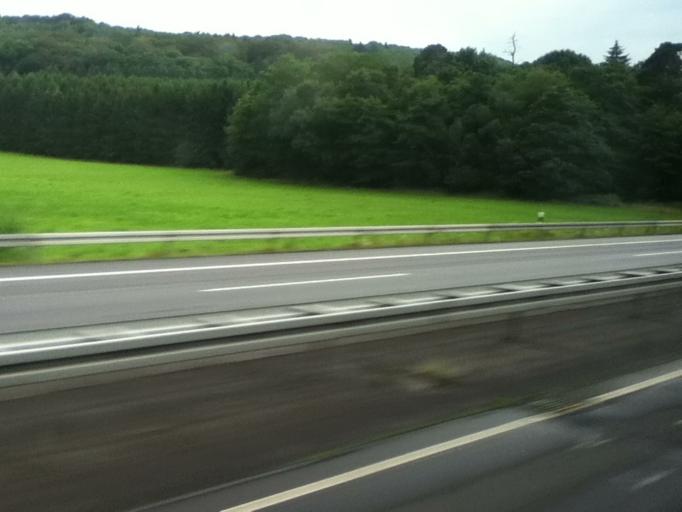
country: DE
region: Hesse
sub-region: Regierungsbezirk Giessen
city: Alten Buseck
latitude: 50.6342
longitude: 8.7386
